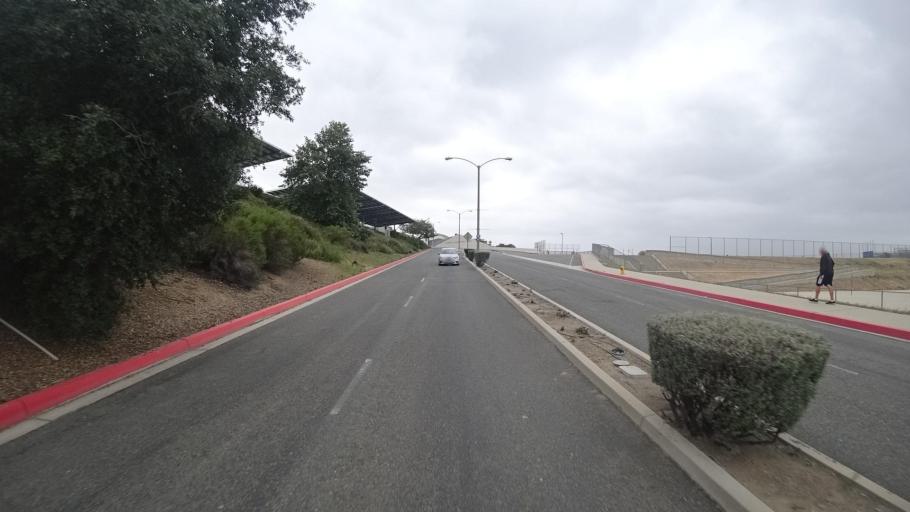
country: US
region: California
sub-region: San Bernardino County
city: Chino Hills
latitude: 34.0223
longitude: -117.7759
